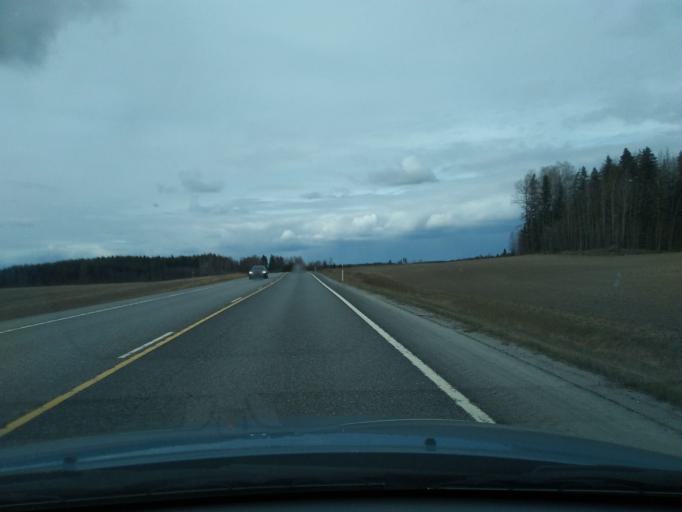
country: FI
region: Uusimaa
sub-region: Porvoo
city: Porvoo
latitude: 60.3998
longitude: 25.5962
